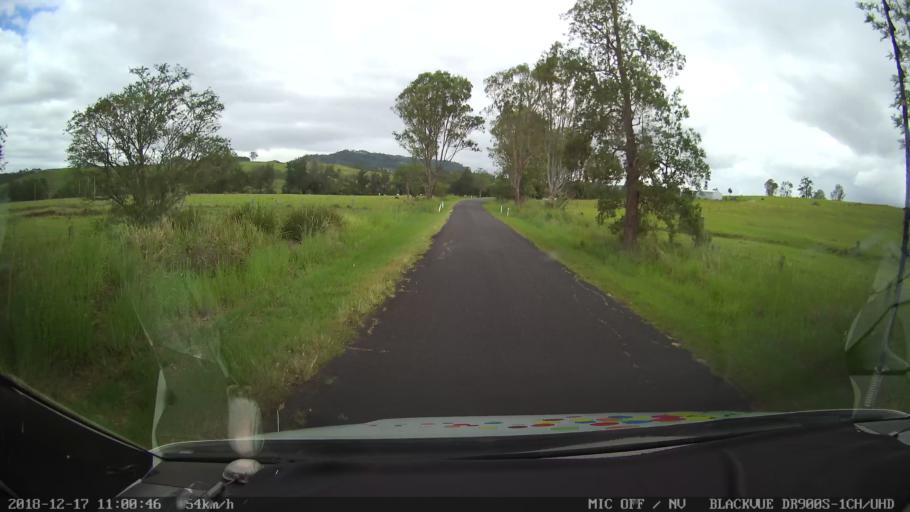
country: AU
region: New South Wales
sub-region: Richmond Valley
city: Casino
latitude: -28.8182
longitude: 152.6208
